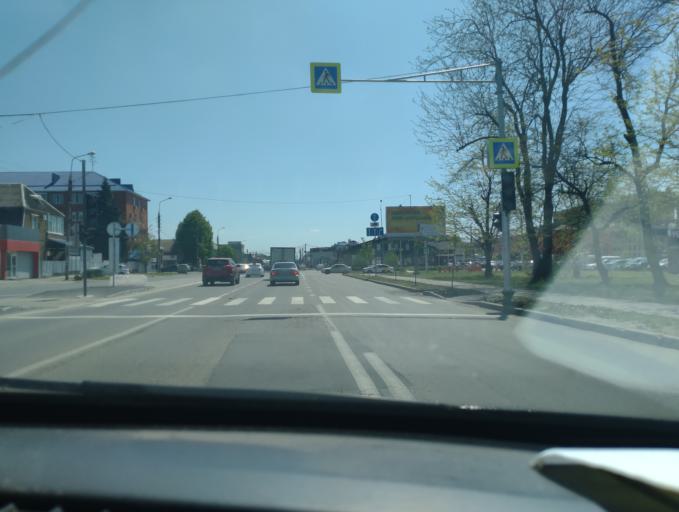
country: RU
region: Krasnodarskiy
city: Krasnodar
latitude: 45.0873
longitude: 39.0142
